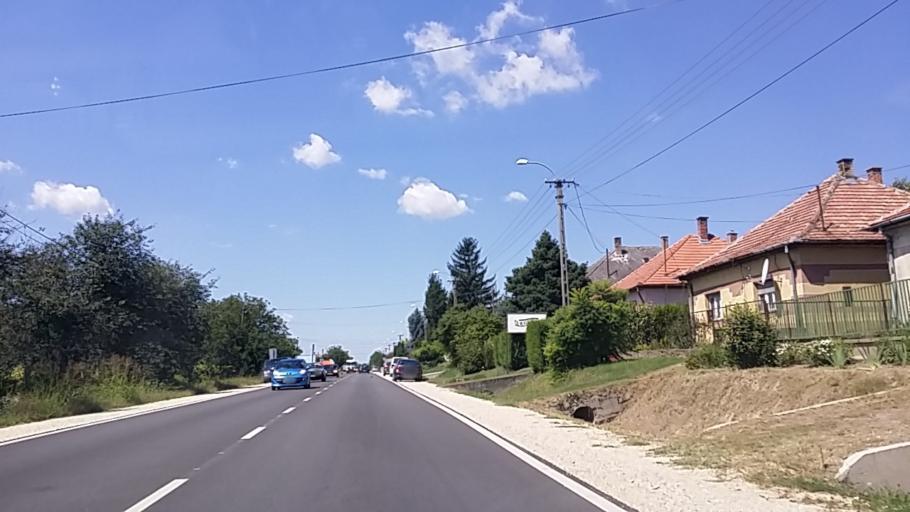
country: HU
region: Tolna
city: Simontornya
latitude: 46.7609
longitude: 18.5379
